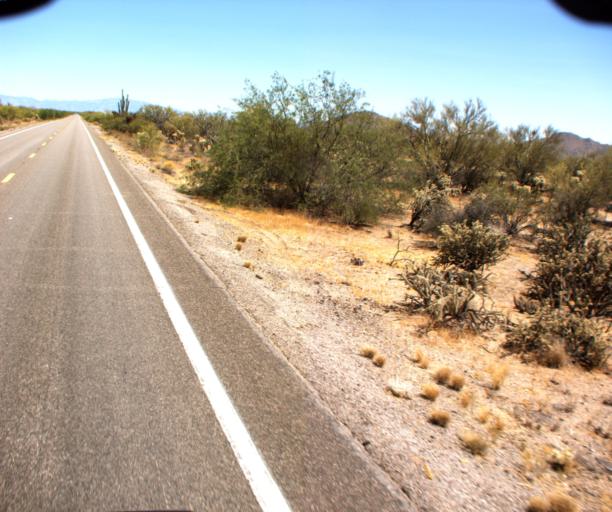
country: US
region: Arizona
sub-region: Pima County
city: Marana
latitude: 32.7672
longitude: -111.1547
